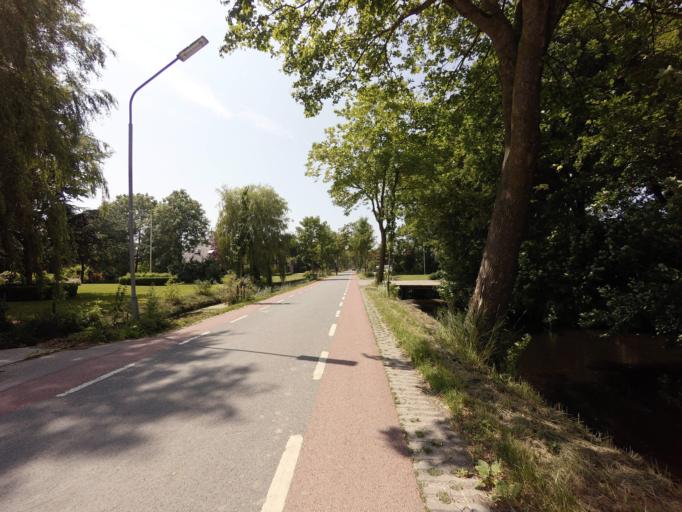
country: NL
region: North Holland
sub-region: Gemeente Opmeer
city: Opmeer
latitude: 52.6531
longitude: 4.9156
